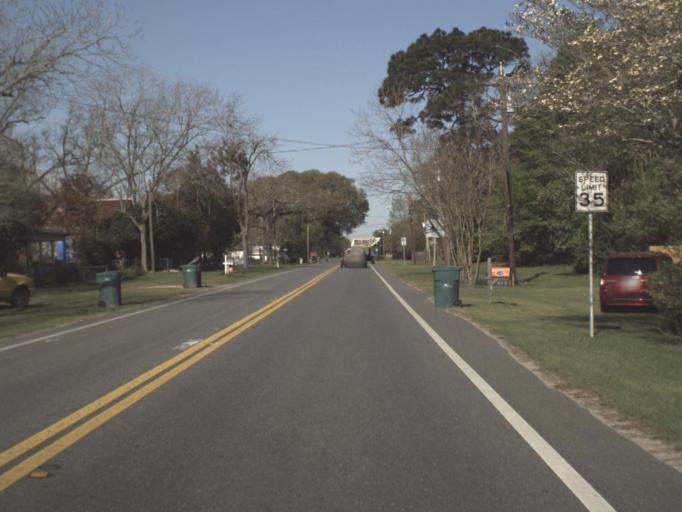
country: US
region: Florida
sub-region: Jackson County
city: Malone
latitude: 30.9579
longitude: -85.1657
